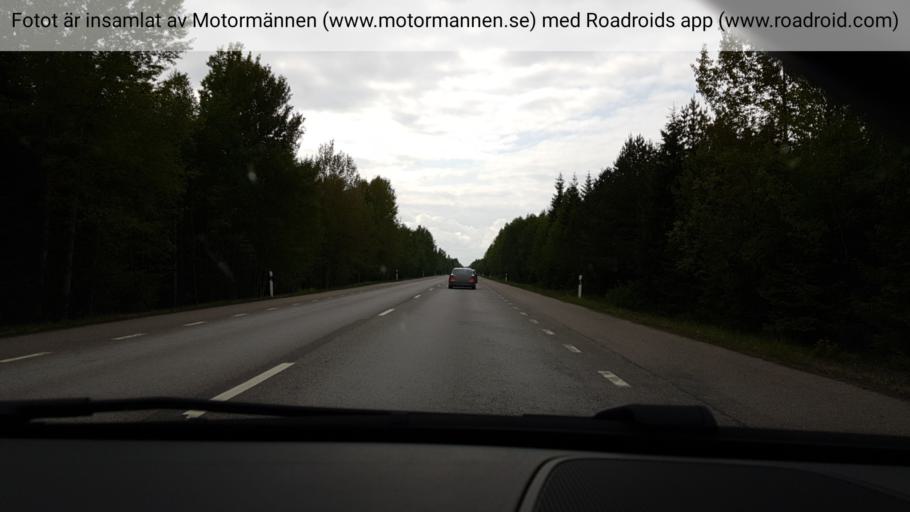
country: SE
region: Uppsala
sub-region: Osthammars Kommun
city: Gimo
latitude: 60.1643
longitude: 18.1072
